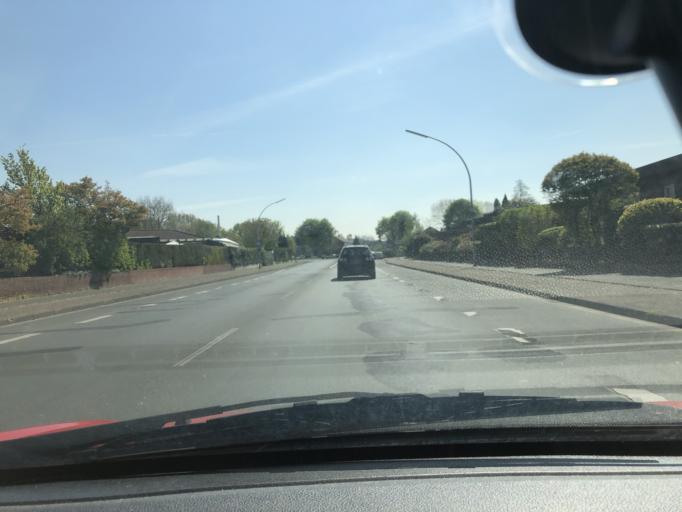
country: DE
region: North Rhine-Westphalia
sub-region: Regierungsbezirk Dusseldorf
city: Kamp-Lintfort
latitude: 51.5006
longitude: 6.5229
